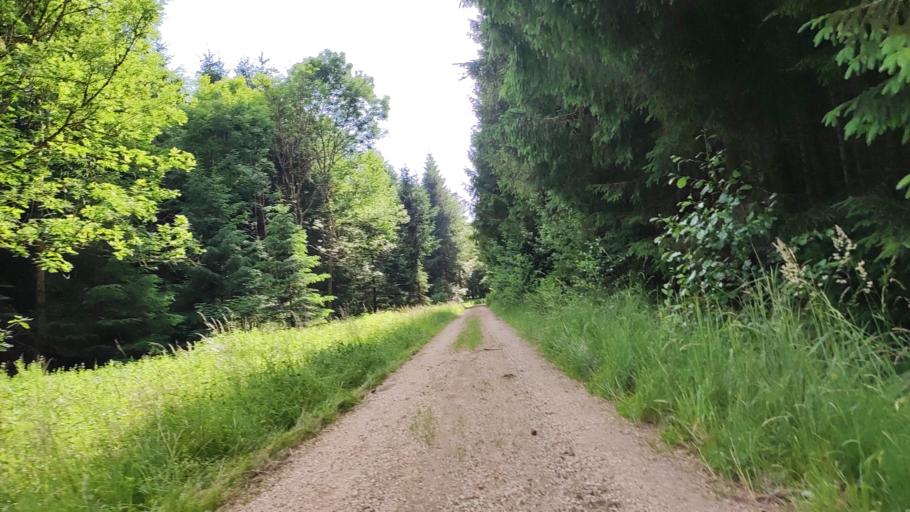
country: DE
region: Bavaria
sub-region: Swabia
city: Landensberg
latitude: 48.4254
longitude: 10.5560
